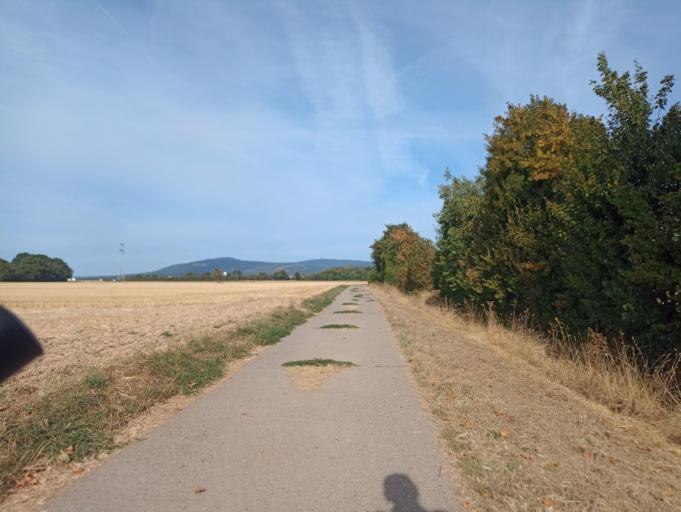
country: DE
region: Hesse
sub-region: Regierungsbezirk Darmstadt
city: Bad Homburg vor der Hoehe
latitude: 50.2071
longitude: 8.6149
